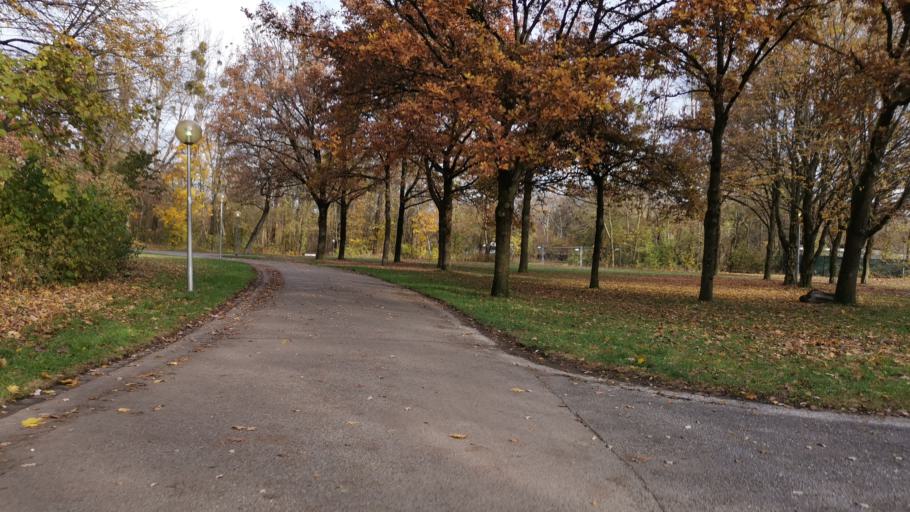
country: DE
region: Bavaria
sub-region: Upper Bavaria
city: Munich
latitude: 48.1674
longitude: 11.5447
